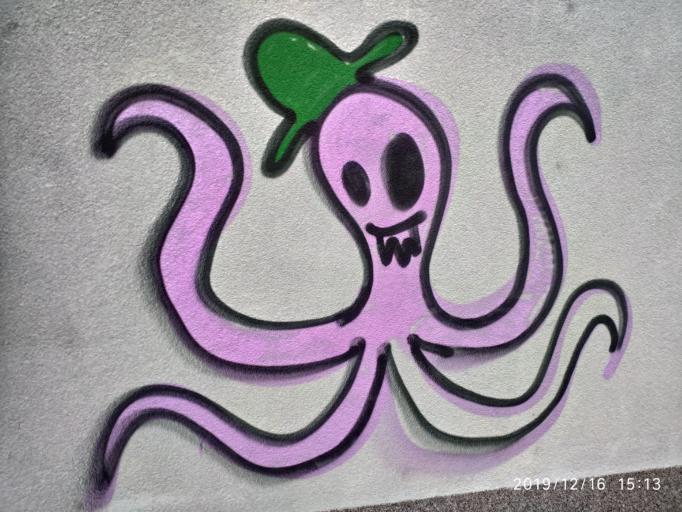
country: PL
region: Lubusz
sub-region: Zielona Gora
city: Zielona Gora
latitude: 51.9402
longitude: 15.4793
